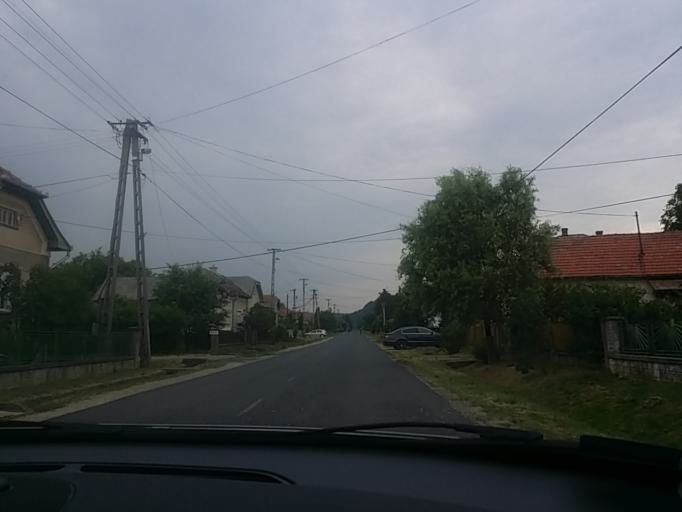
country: HU
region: Borsod-Abauj-Zemplen
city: Arlo
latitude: 48.2249
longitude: 20.1976
